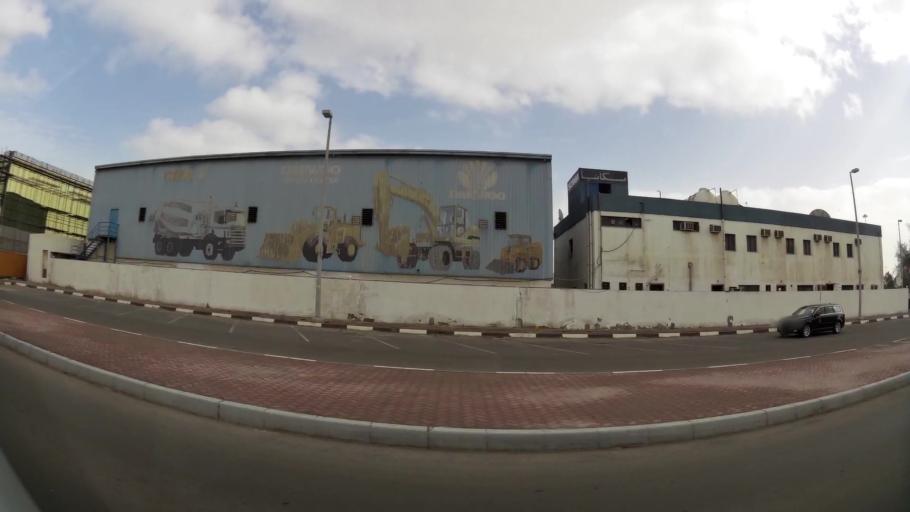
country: AE
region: Abu Dhabi
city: Abu Dhabi
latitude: 24.4138
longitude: 54.4998
